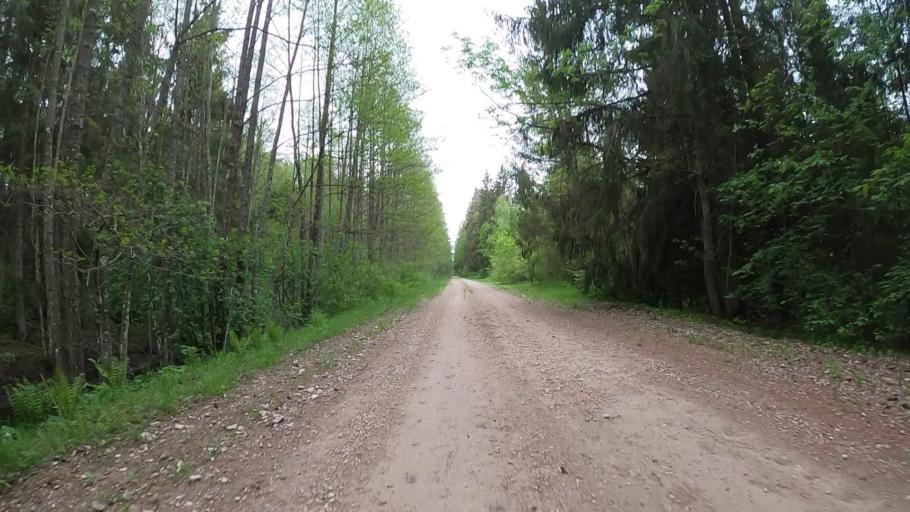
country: LV
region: Ozolnieku
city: Ozolnieki
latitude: 56.7999
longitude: 23.7834
